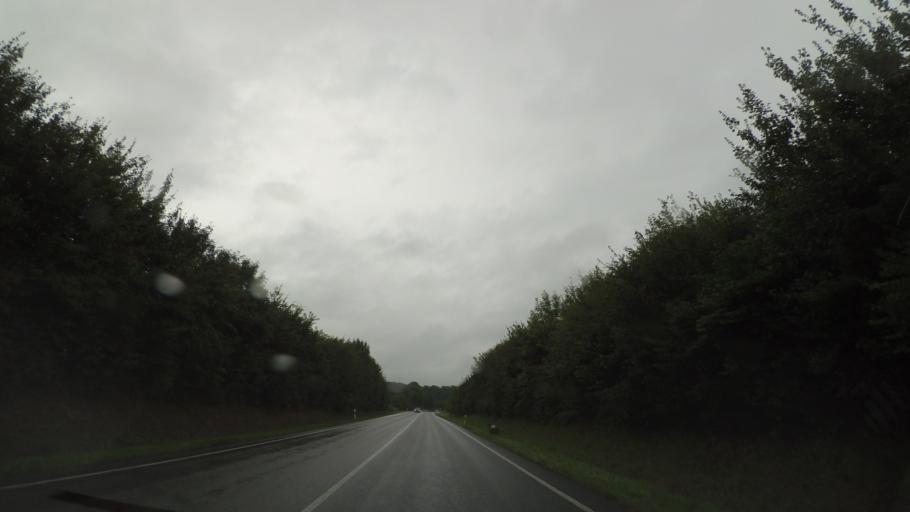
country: DE
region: Baden-Wuerttemberg
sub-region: Regierungsbezirk Stuttgart
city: Untermunkheim
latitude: 49.1731
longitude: 9.7250
